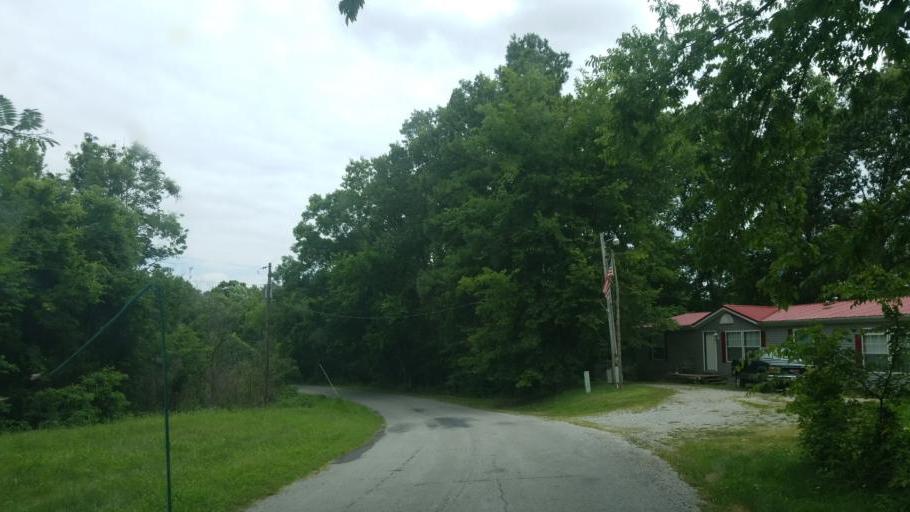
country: US
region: Illinois
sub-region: Jackson County
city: Murphysboro
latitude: 37.6765
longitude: -89.3922
